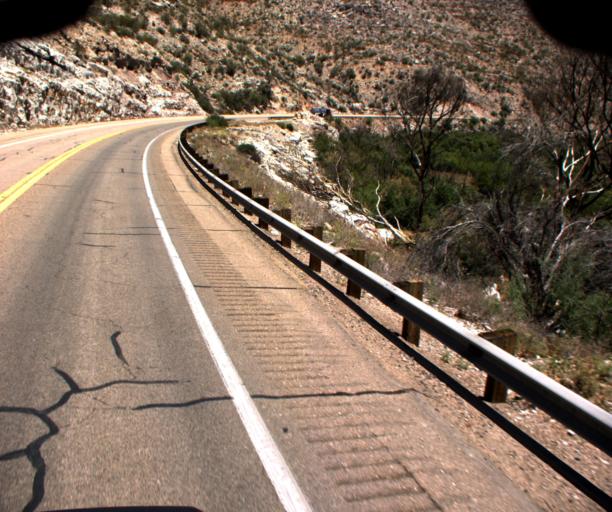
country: US
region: Arizona
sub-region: Pinal County
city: Kearny
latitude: 33.0037
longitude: -110.7652
